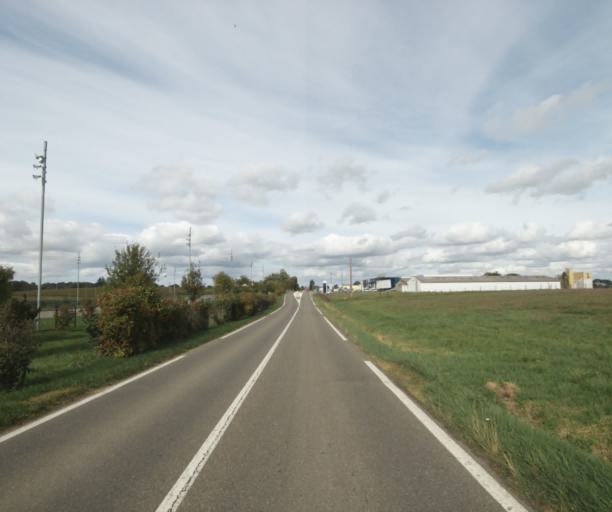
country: FR
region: Midi-Pyrenees
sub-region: Departement du Gers
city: Eauze
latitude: 43.8382
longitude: 0.0927
